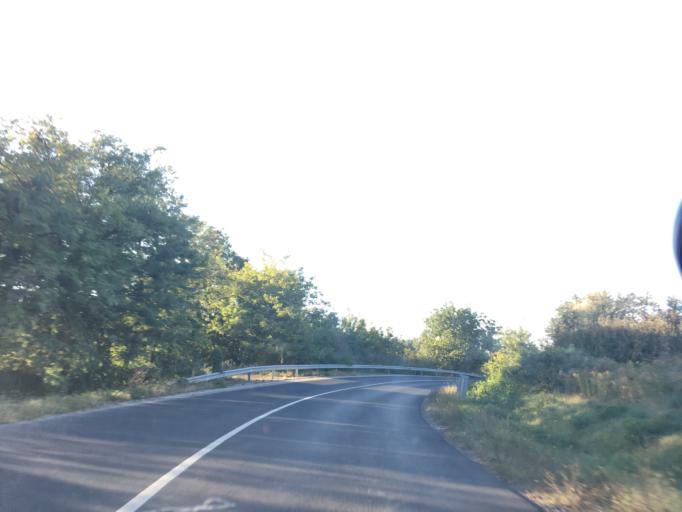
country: HU
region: Pest
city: Szazhalombatta
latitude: 47.3306
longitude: 18.8946
